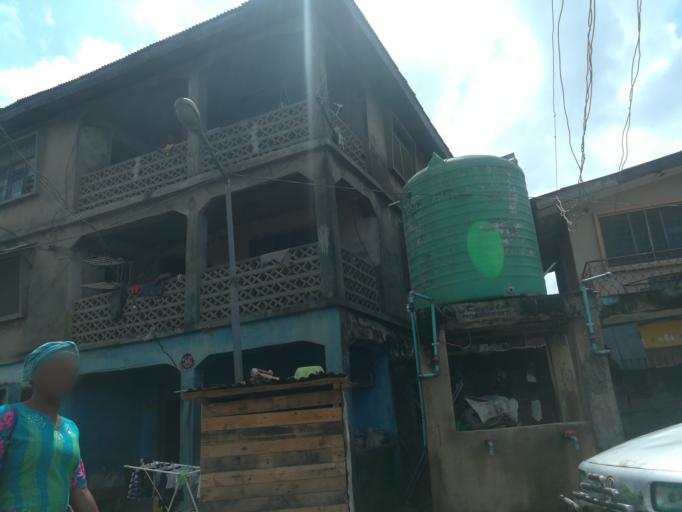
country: NG
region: Lagos
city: Mushin
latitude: 6.5346
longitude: 3.3633
